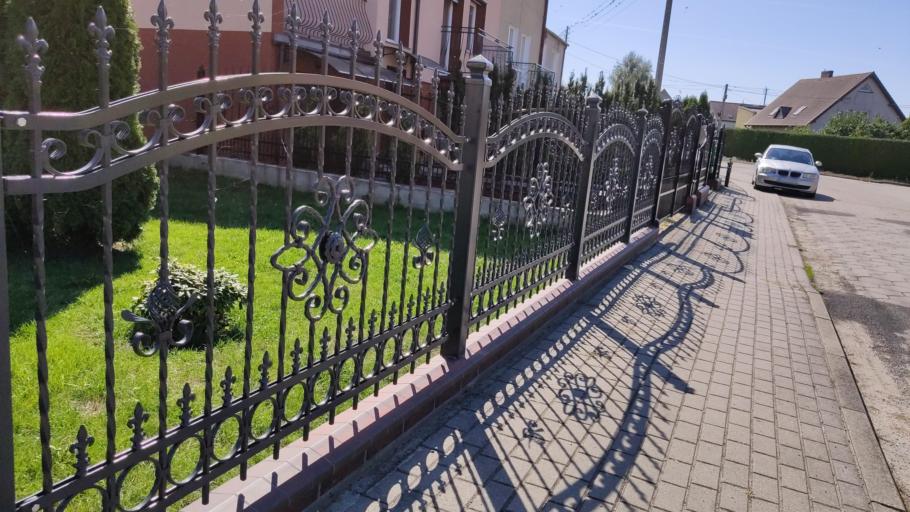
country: PL
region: Kujawsko-Pomorskie
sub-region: Powiat zninski
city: Znin
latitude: 52.8478
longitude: 17.7522
